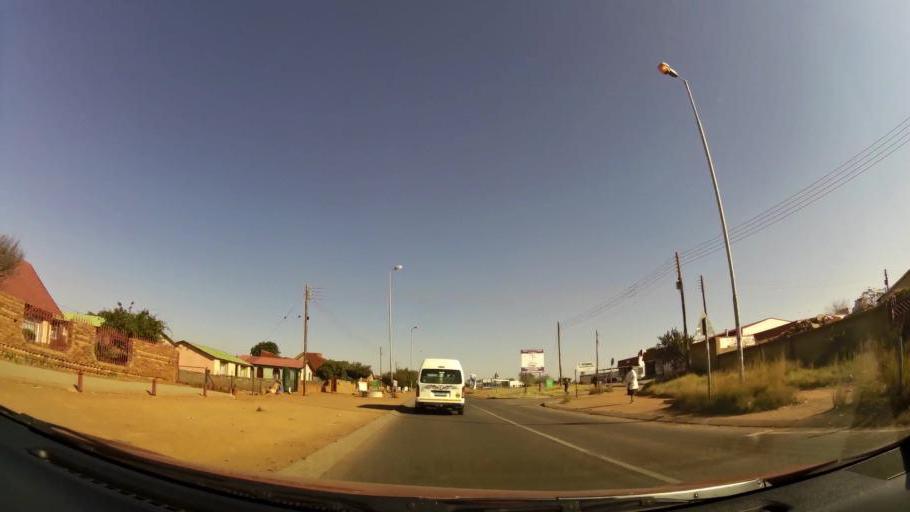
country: ZA
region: Gauteng
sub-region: City of Tshwane Metropolitan Municipality
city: Mabopane
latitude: -25.5388
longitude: 28.1058
